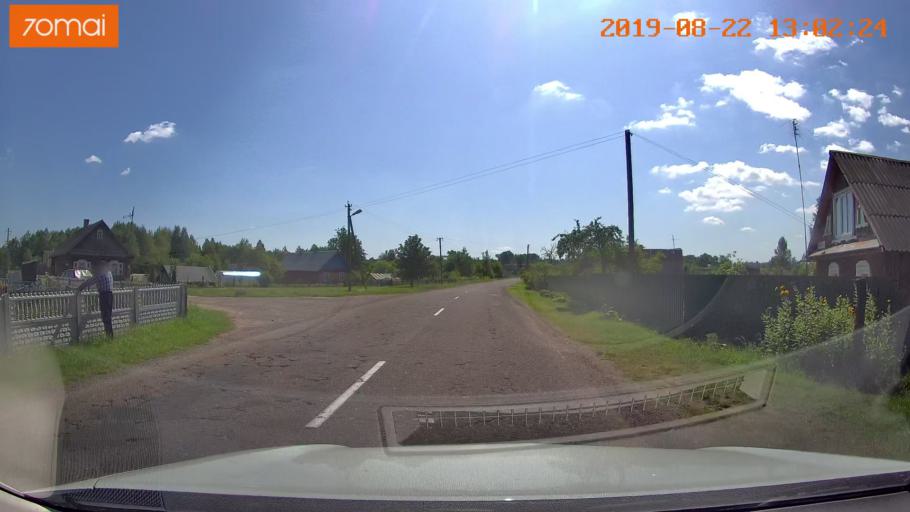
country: BY
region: Minsk
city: Prawdzinski
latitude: 53.3890
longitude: 27.8254
